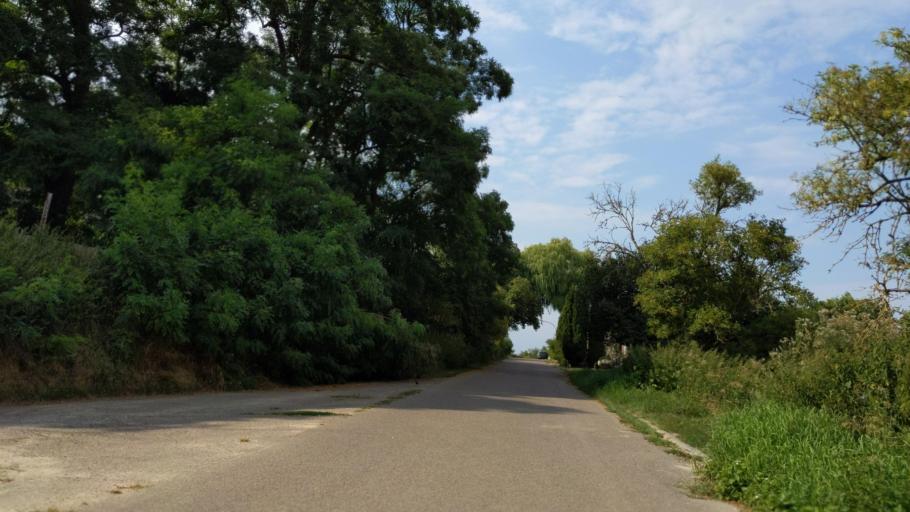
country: DE
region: Schleswig-Holstein
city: Behlendorf
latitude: 53.6923
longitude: 10.6717
